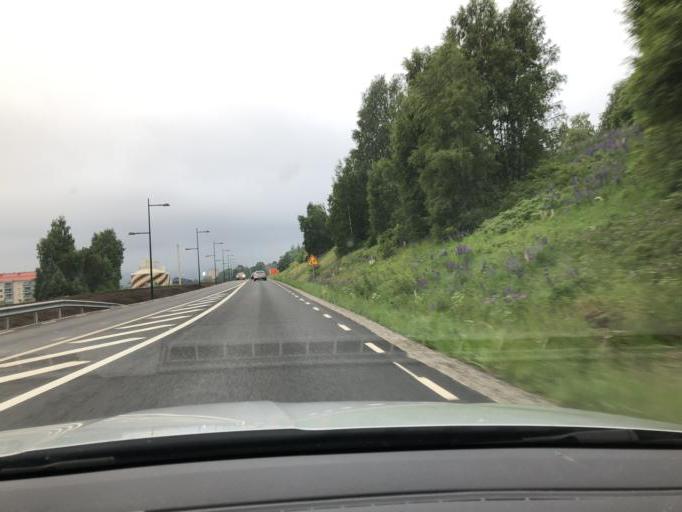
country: SE
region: Vaesternorrland
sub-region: Sundsvalls Kommun
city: Sundsvall
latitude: 62.3952
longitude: 17.3248
